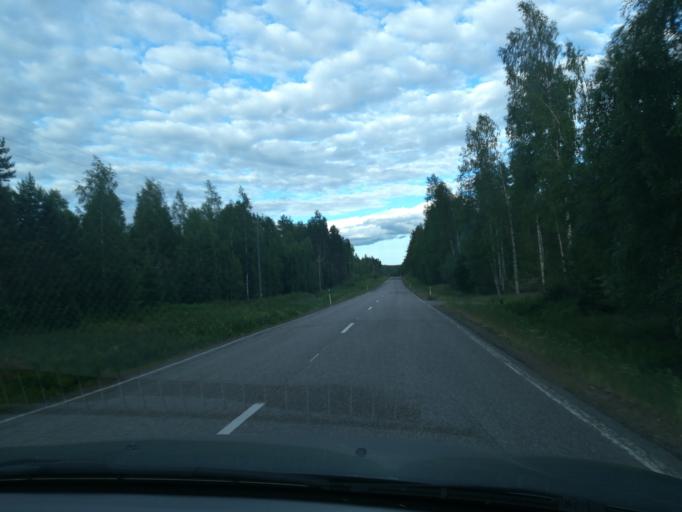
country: FI
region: Southern Savonia
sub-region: Mikkeli
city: Puumala
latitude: 61.5602
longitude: 28.0163
